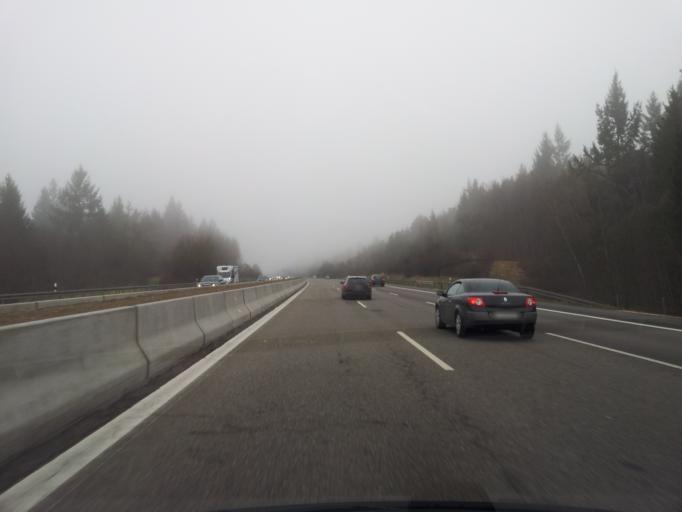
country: DE
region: Baden-Wuerttemberg
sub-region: Freiburg Region
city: Muhlhausen-Ehingen
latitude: 47.8438
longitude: 8.8127
